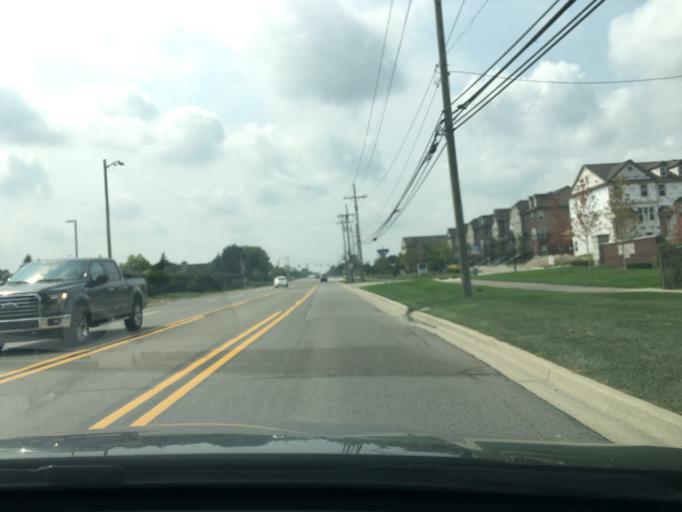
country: US
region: Michigan
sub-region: Oakland County
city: Rochester Hills
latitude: 42.6365
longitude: -83.1216
